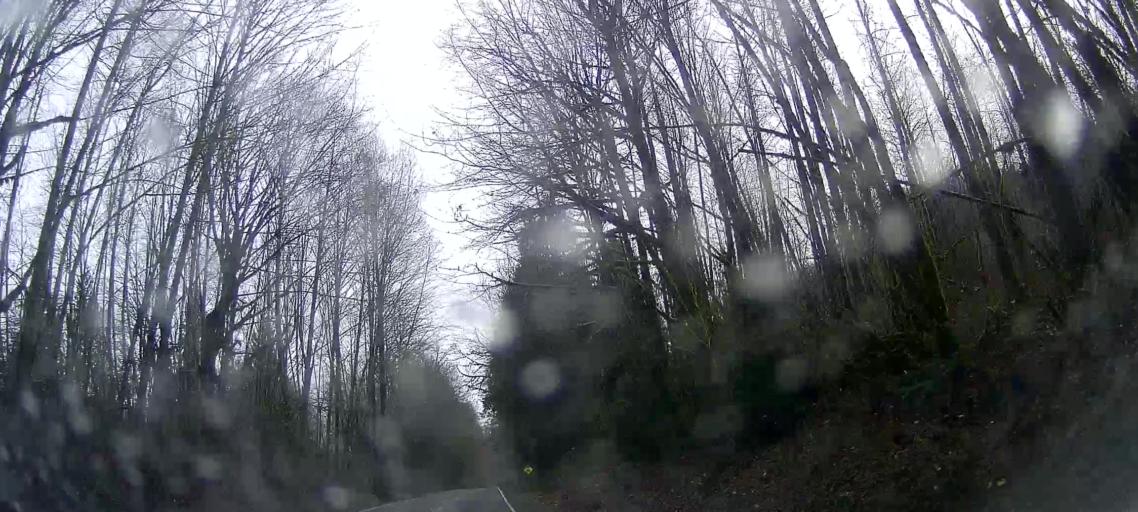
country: US
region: Washington
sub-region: Snohomish County
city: Darrington
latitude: 48.5302
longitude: -121.7856
